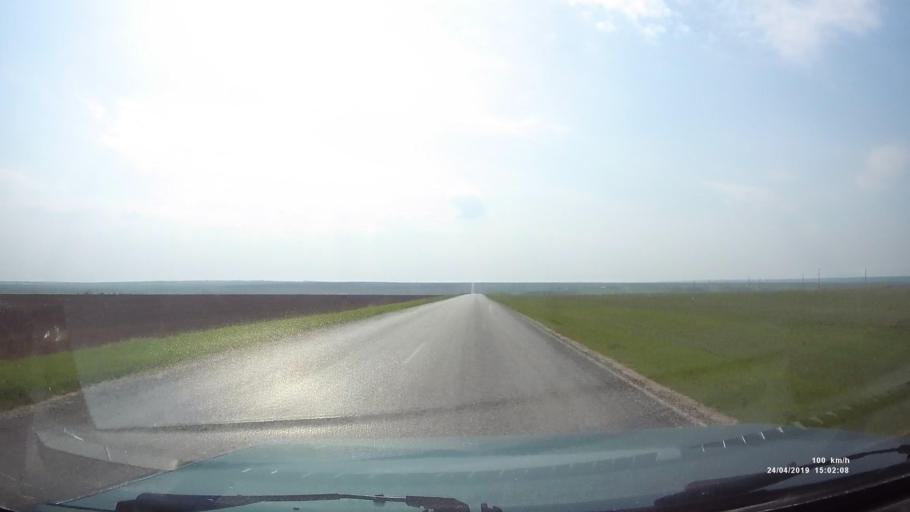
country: RU
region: Rostov
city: Remontnoye
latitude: 46.5664
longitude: 43.5185
